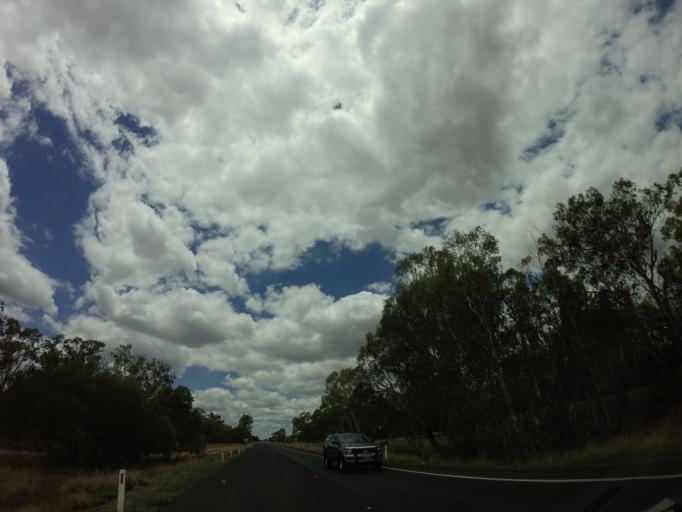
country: AU
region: Queensland
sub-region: Goondiwindi
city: Goondiwindi
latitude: -28.1590
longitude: 150.6579
